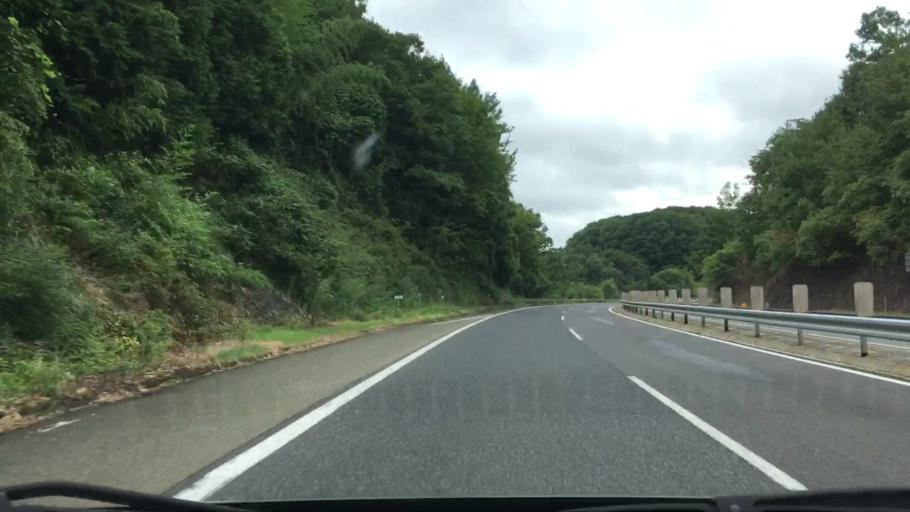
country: JP
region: Hiroshima
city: Shobara
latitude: 34.8277
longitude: 133.0524
